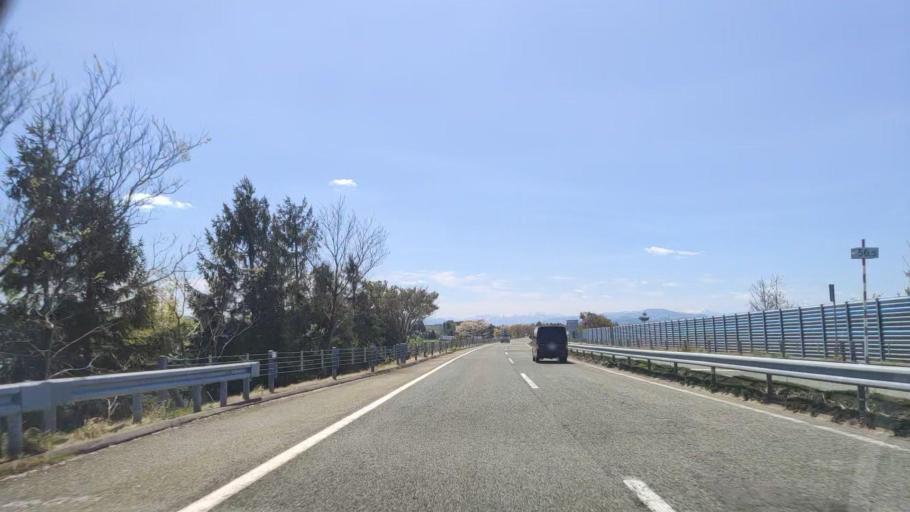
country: JP
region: Akita
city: Yokotemachi
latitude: 39.3216
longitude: 140.5147
